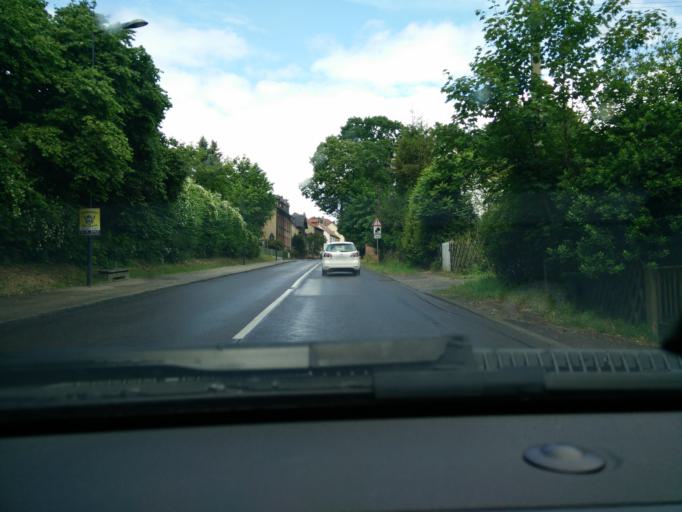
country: DE
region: Saxony
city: Grimma
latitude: 51.2453
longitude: 12.7309
